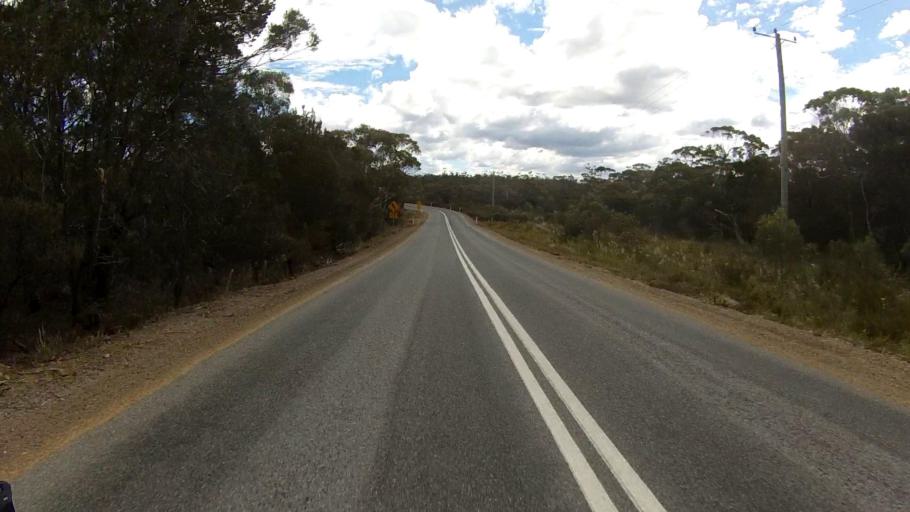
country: AU
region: Tasmania
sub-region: Break O'Day
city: St Helens
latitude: -41.9808
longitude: 148.1388
